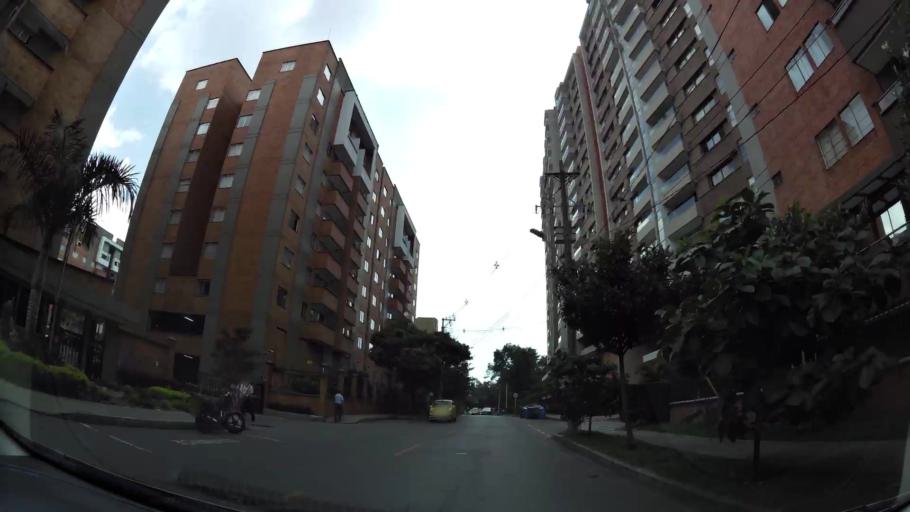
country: CO
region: Antioquia
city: Envigado
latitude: 6.1798
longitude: -75.5864
